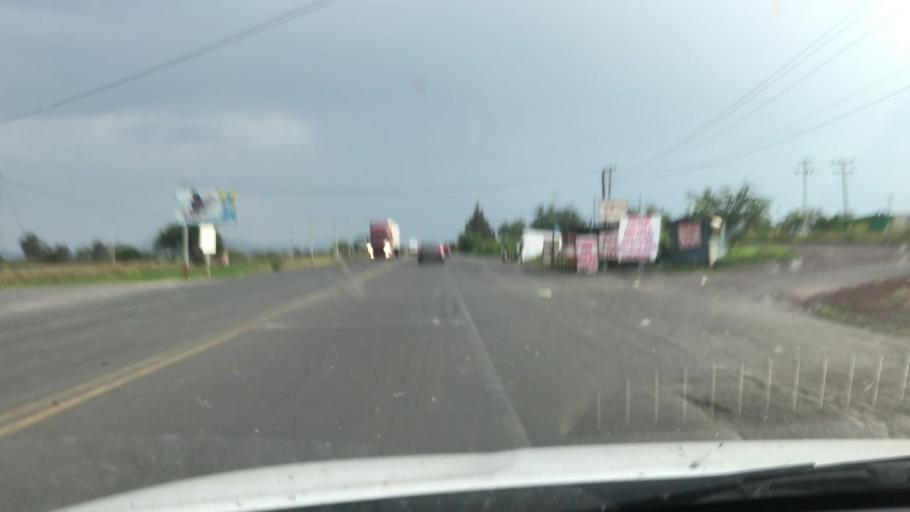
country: MX
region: Michoacan
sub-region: Yurecuaro
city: Yurecuaro
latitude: 20.3181
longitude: -102.3034
